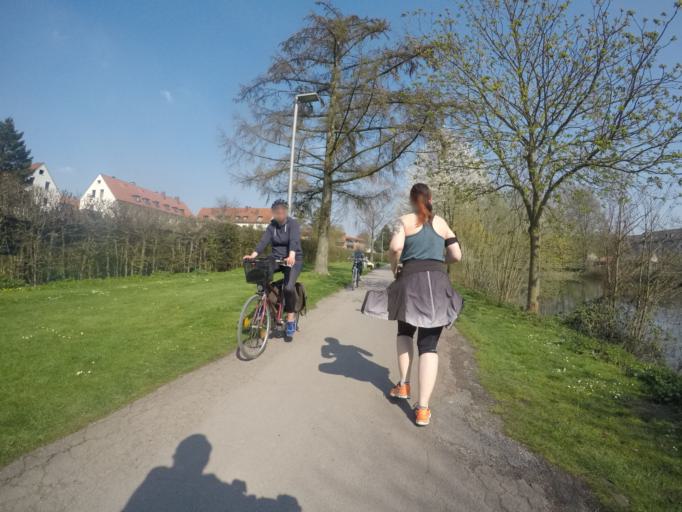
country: DE
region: North Rhine-Westphalia
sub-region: Regierungsbezirk Detmold
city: Bielefeld
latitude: 52.0266
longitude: 8.5751
